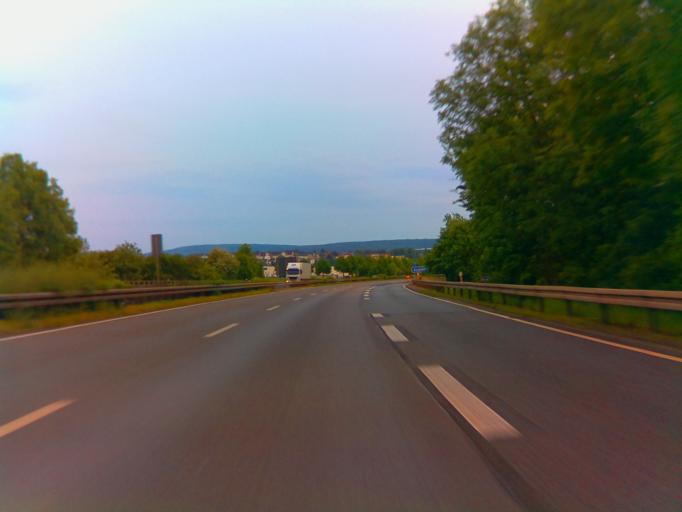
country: DE
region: Hesse
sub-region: Regierungsbezirk Kassel
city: Lohfelden
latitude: 51.2845
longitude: 9.5184
